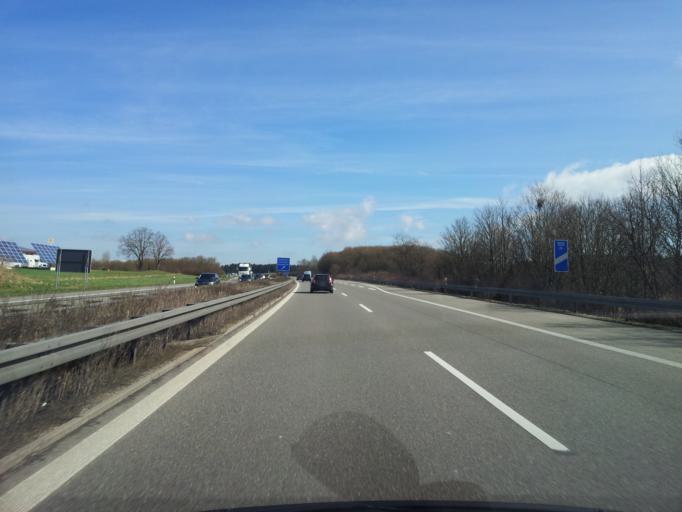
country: DE
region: Baden-Wuerttemberg
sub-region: Karlsruhe Region
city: Empfingen
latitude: 48.3830
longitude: 8.7230
